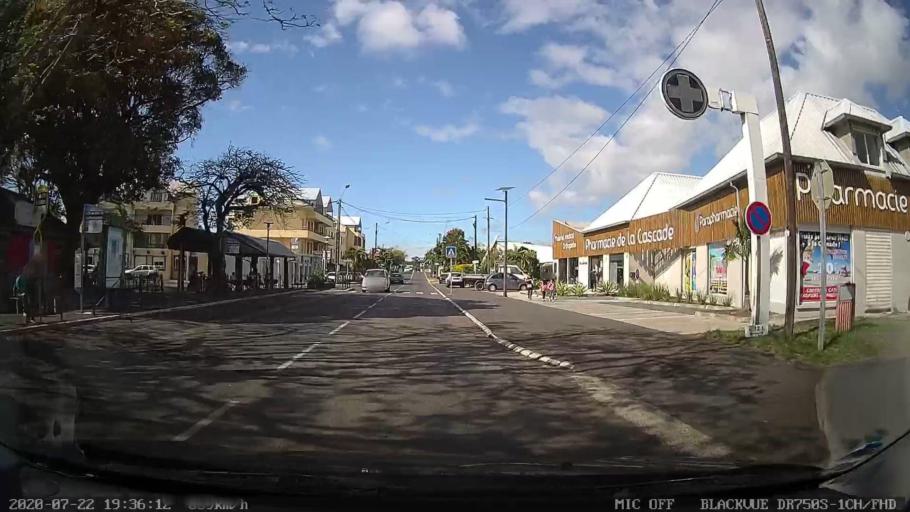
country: RE
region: Reunion
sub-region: Reunion
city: Sainte-Suzanne
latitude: -20.9064
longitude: 55.6076
